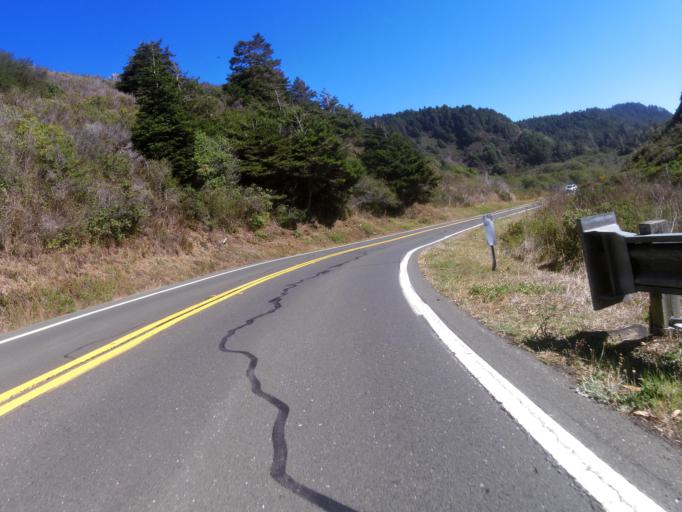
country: US
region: California
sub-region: Mendocino County
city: Boonville
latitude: 39.1061
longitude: -123.7023
